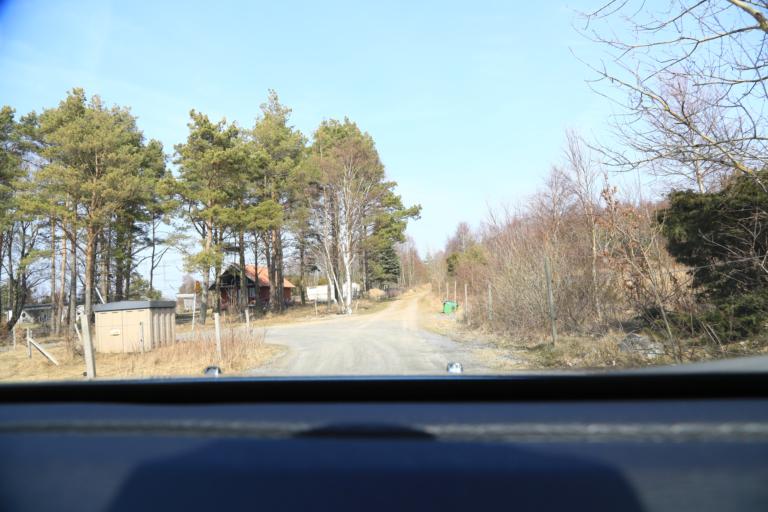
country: SE
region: Halland
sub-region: Kungsbacka Kommun
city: Frillesas
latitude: 57.2651
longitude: 12.1272
